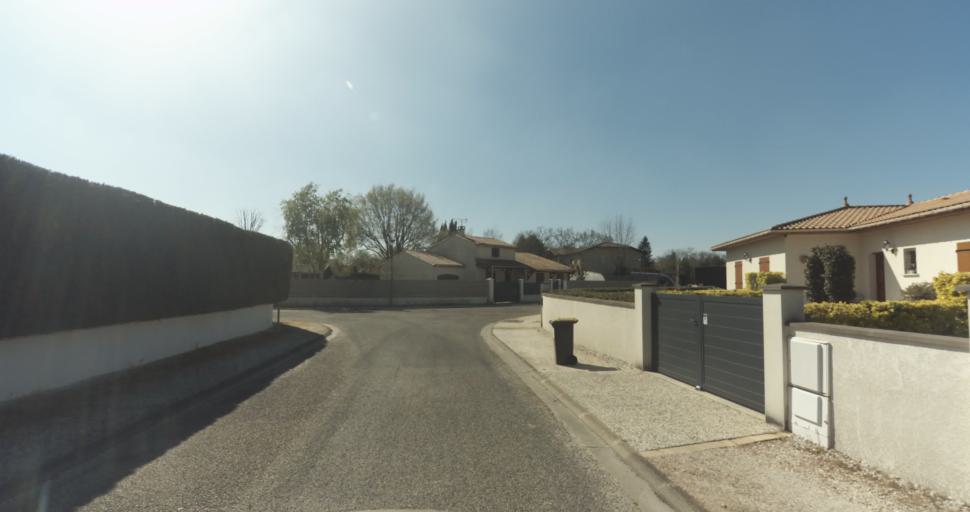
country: FR
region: Aquitaine
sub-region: Departement de la Gironde
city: Martignas-sur-Jalle
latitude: 44.8079
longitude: -0.7813
